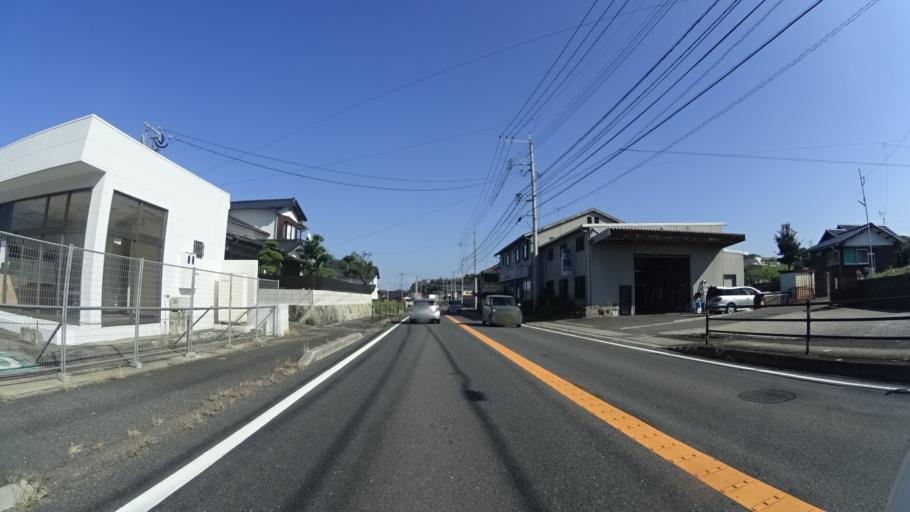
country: JP
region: Fukuoka
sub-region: Buzen-shi
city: Buzen
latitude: 33.6238
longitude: 131.0911
